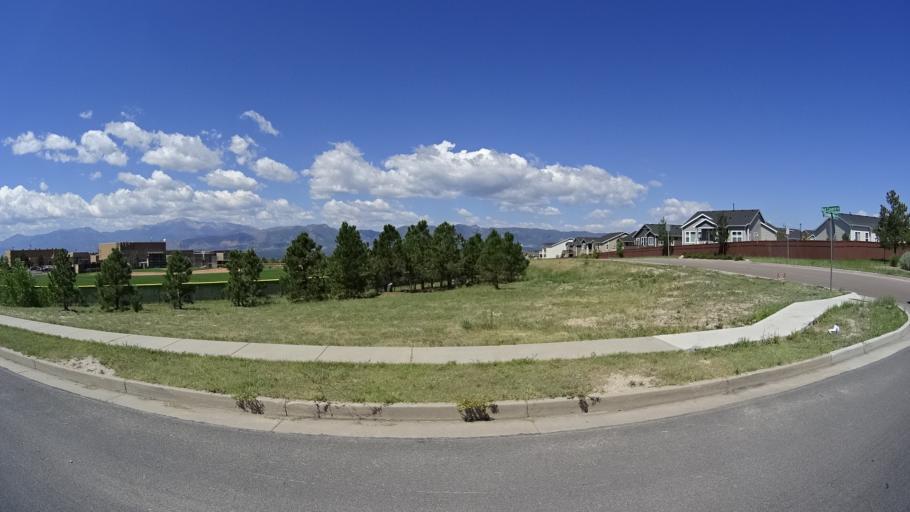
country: US
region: Colorado
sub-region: El Paso County
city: Black Forest
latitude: 38.9890
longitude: -104.7604
